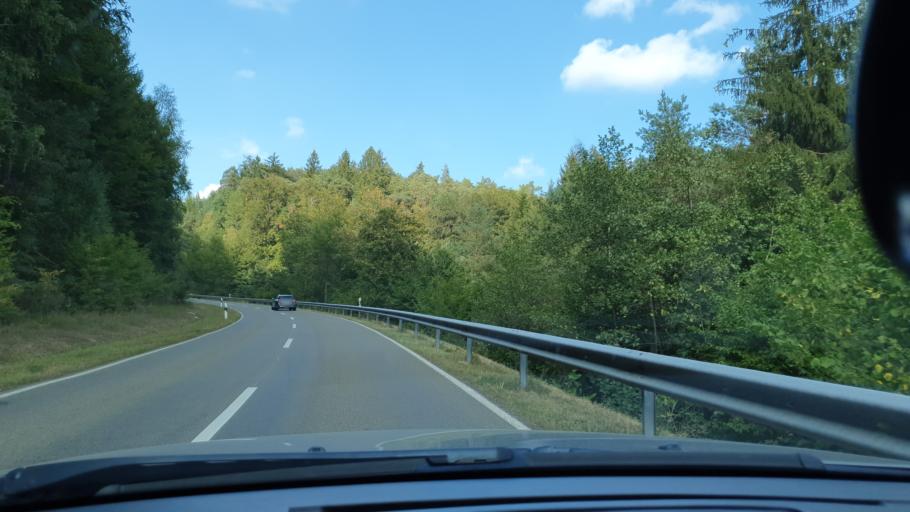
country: DE
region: Rheinland-Pfalz
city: Stelzenberg
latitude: 49.3713
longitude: 7.7266
